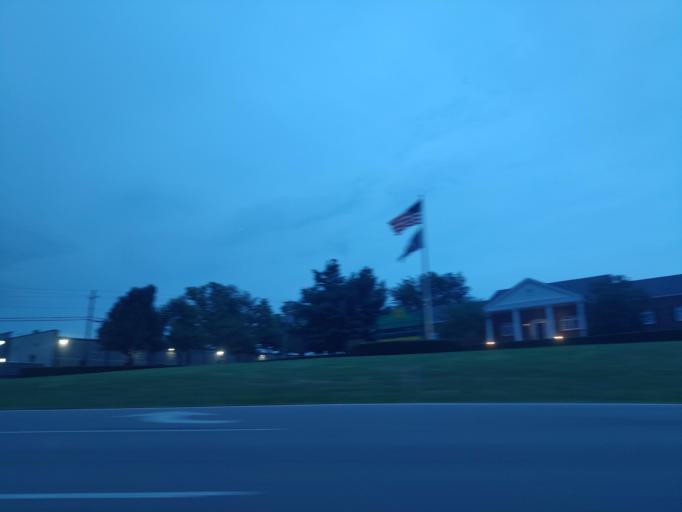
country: US
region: Kentucky
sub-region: Scott County
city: Georgetown
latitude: 38.2302
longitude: -84.5341
